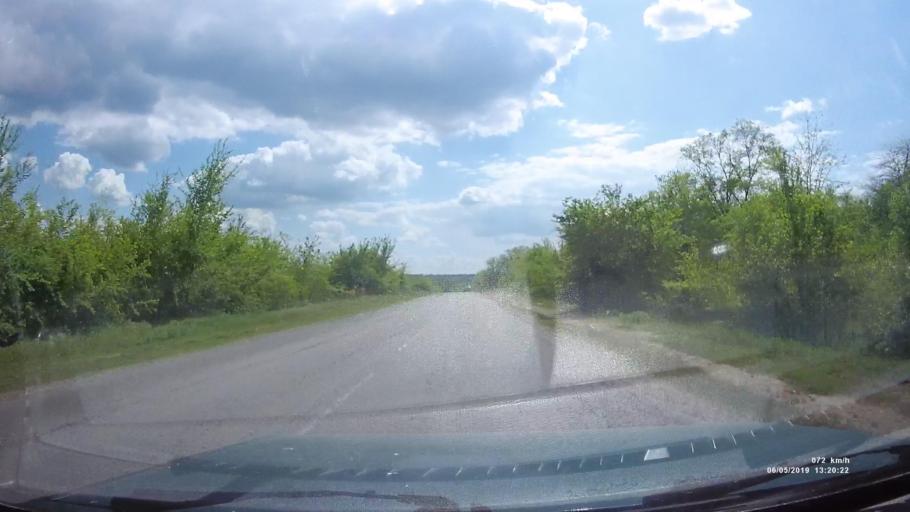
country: RU
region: Rostov
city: Ust'-Donetskiy
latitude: 47.7169
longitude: 40.9112
